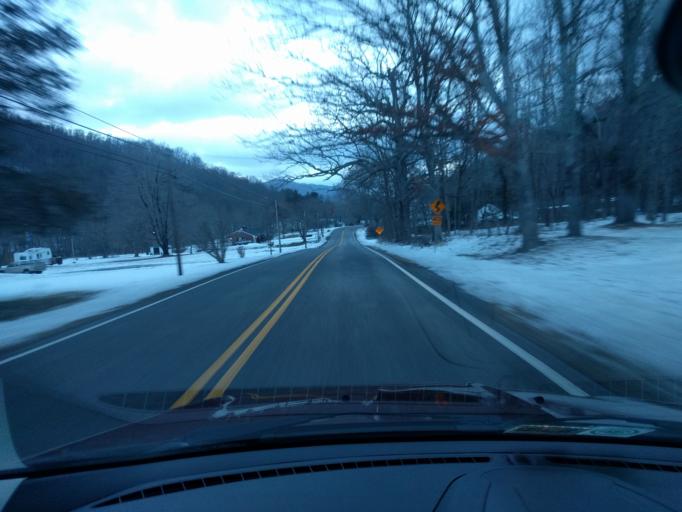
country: US
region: Virginia
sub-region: Alleghany County
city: Clifton Forge
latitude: 37.9393
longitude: -79.8769
